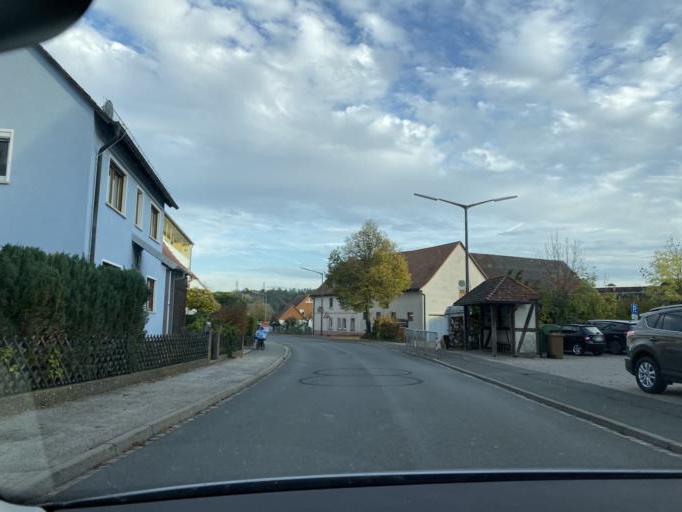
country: DE
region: Bavaria
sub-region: Regierungsbezirk Mittelfranken
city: Puschendorf
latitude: 49.5236
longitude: 10.8300
